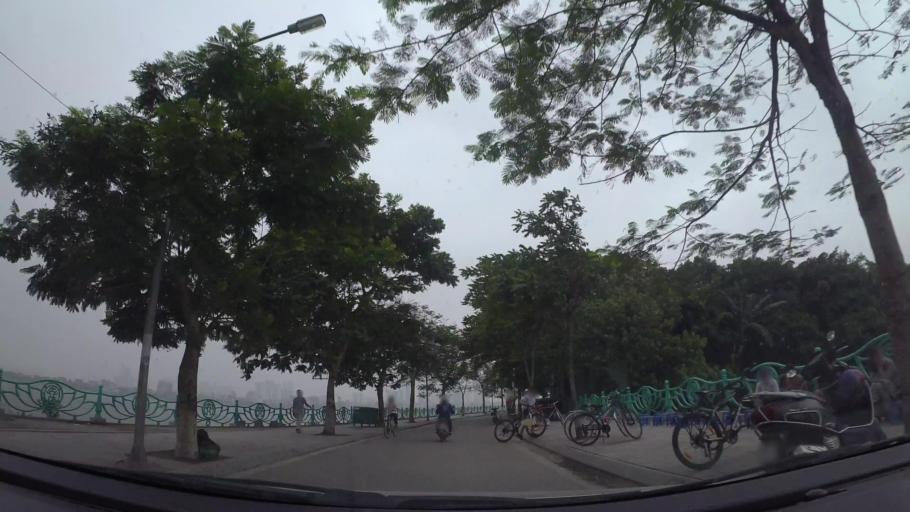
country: VN
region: Ha Noi
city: Tay Ho
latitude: 21.0591
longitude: 105.8188
